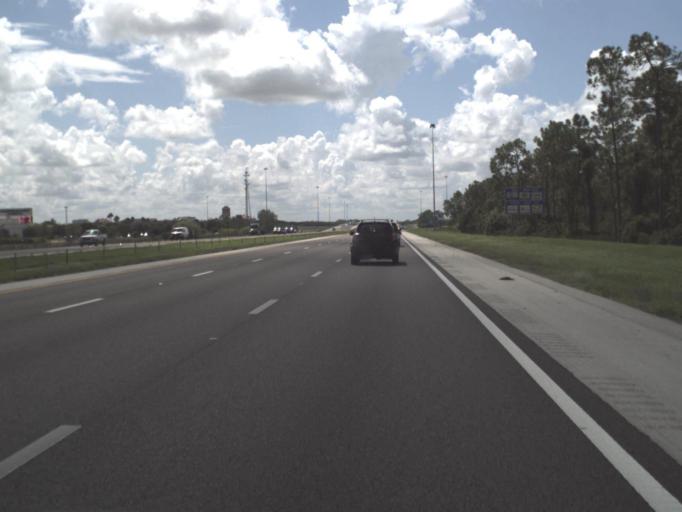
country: US
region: Florida
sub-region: Lee County
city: Estero
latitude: 26.4411
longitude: -81.7812
